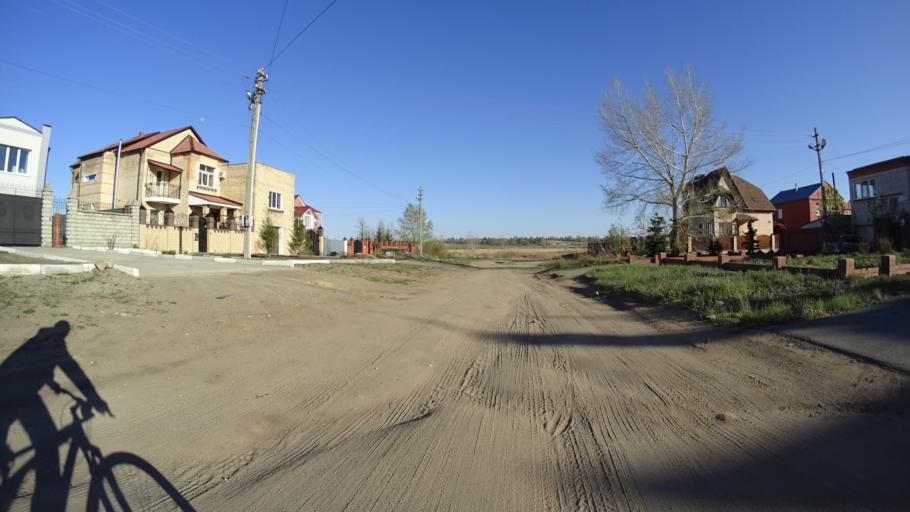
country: RU
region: Chelyabinsk
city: Troitsk
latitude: 54.0698
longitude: 61.5375
